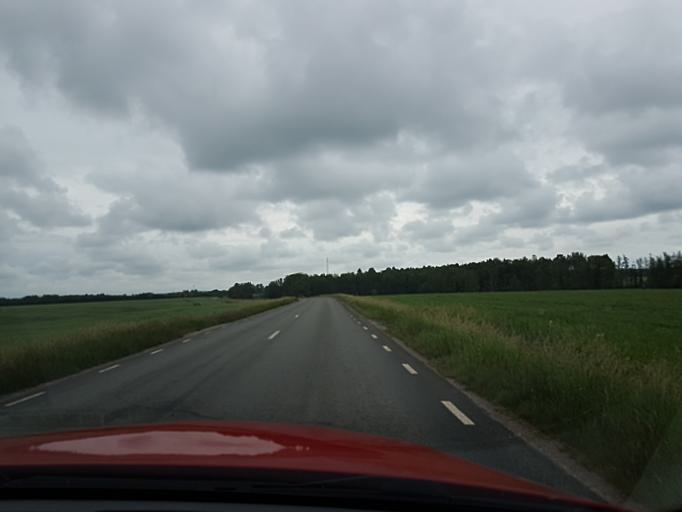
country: SE
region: Vaestra Goetaland
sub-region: Tidaholms Kommun
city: Olofstorp
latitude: 58.2972
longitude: 14.0610
